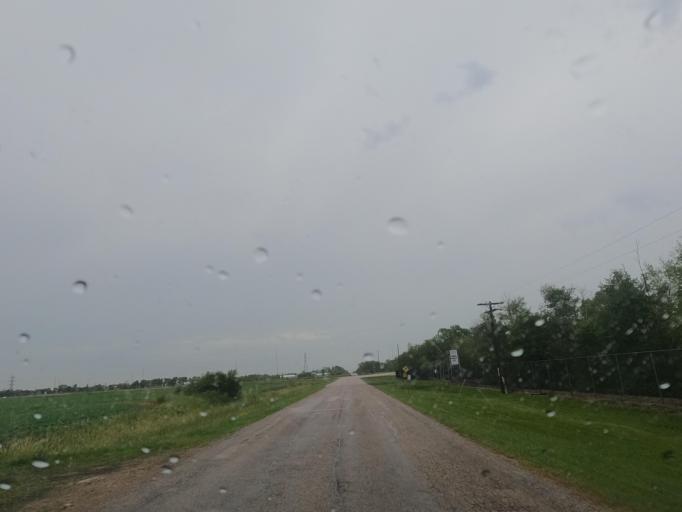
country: CA
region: Manitoba
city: Winnipeg
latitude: 49.8363
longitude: -96.9812
